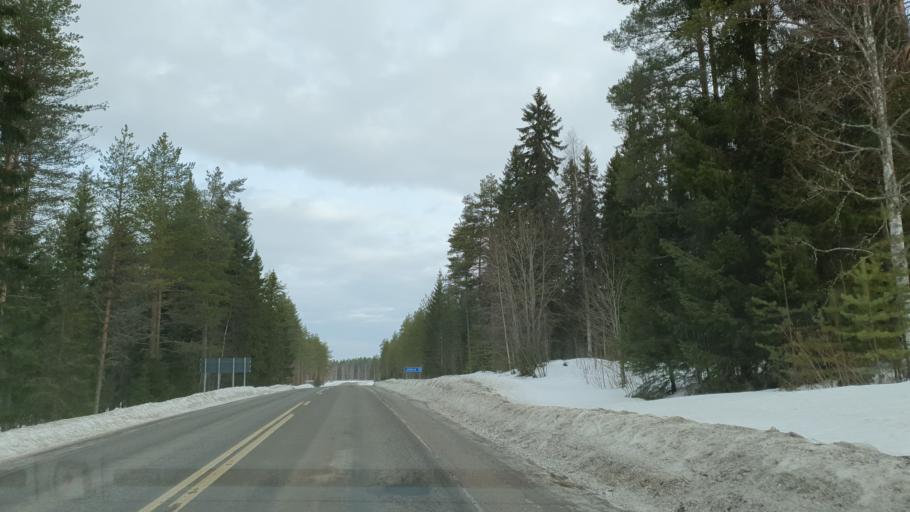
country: FI
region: Kainuu
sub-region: Kajaani
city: Vuokatti
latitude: 64.2271
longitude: 28.0666
